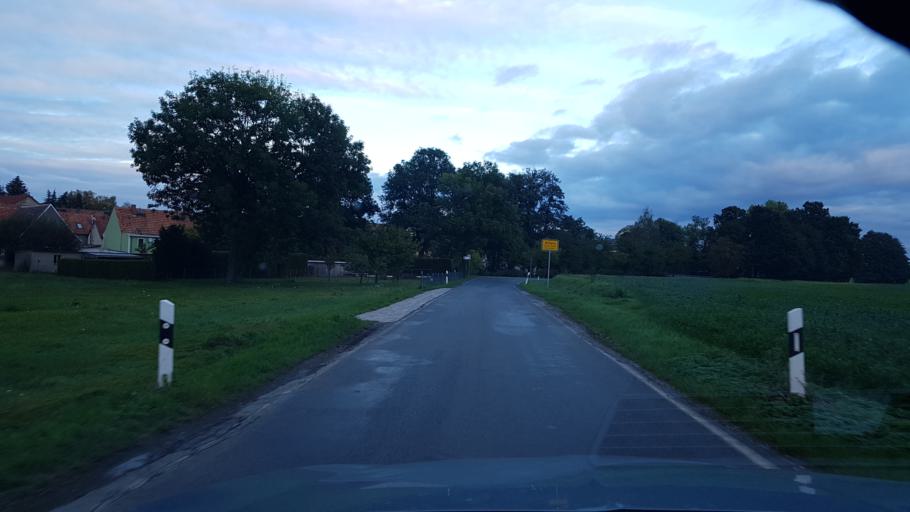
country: DE
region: Saxony
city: Priestewitz
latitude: 51.2402
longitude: 13.5614
